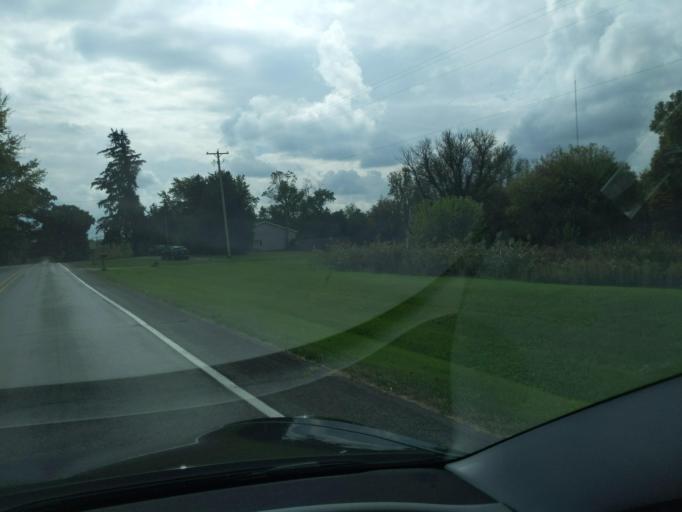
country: US
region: Michigan
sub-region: Eaton County
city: Eaton Rapids
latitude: 42.4497
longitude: -84.5606
